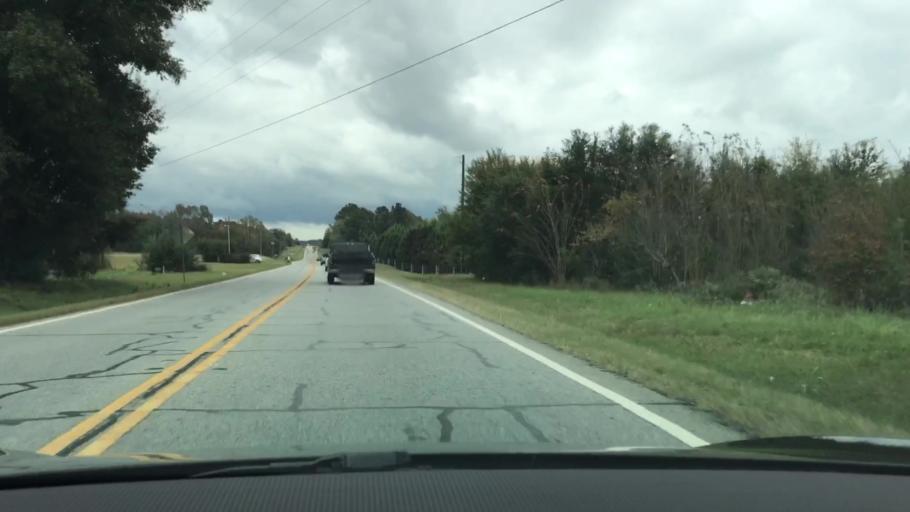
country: US
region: Georgia
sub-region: Oconee County
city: Watkinsville
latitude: 33.8361
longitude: -83.3826
